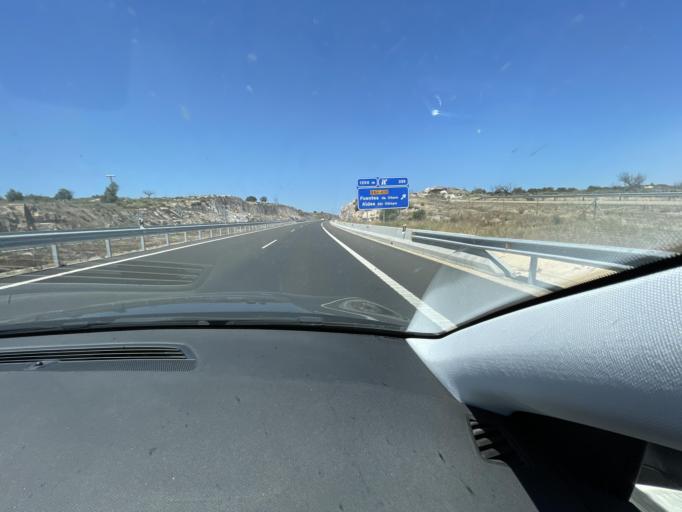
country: ES
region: Castille and Leon
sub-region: Provincia de Salamanca
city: Fuentes de Onoro
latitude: 40.5985
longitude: -6.8101
